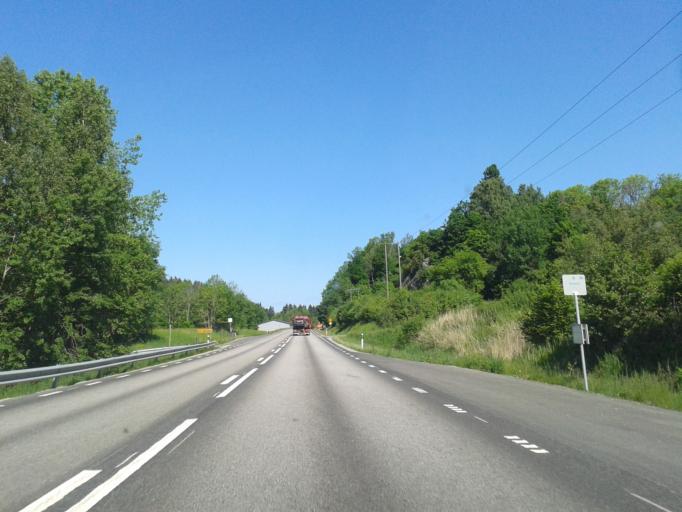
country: SE
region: Vaestra Goetaland
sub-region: Orust
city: Henan
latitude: 58.2199
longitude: 11.6884
